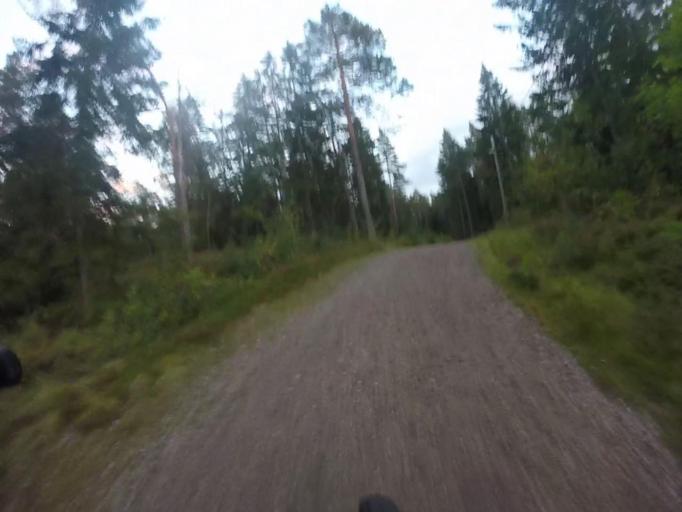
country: SE
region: Vaestra Goetaland
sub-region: Trollhattan
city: Trollhattan
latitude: 58.2943
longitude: 12.2598
